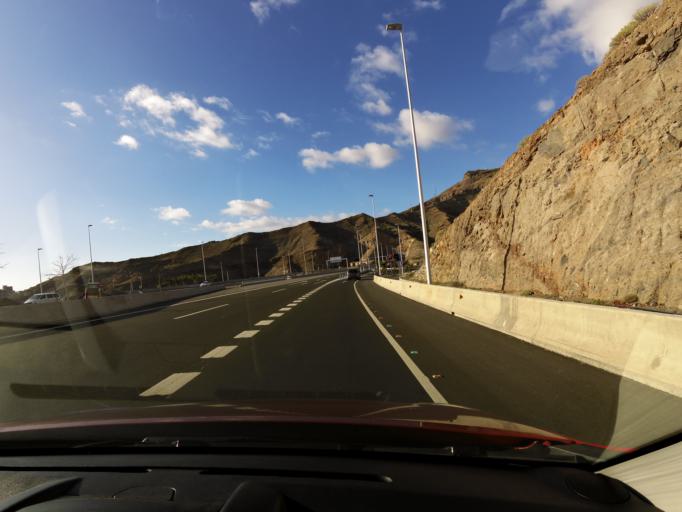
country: ES
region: Canary Islands
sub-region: Provincia de Las Palmas
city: Puerto Rico
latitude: 27.8009
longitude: -15.7057
